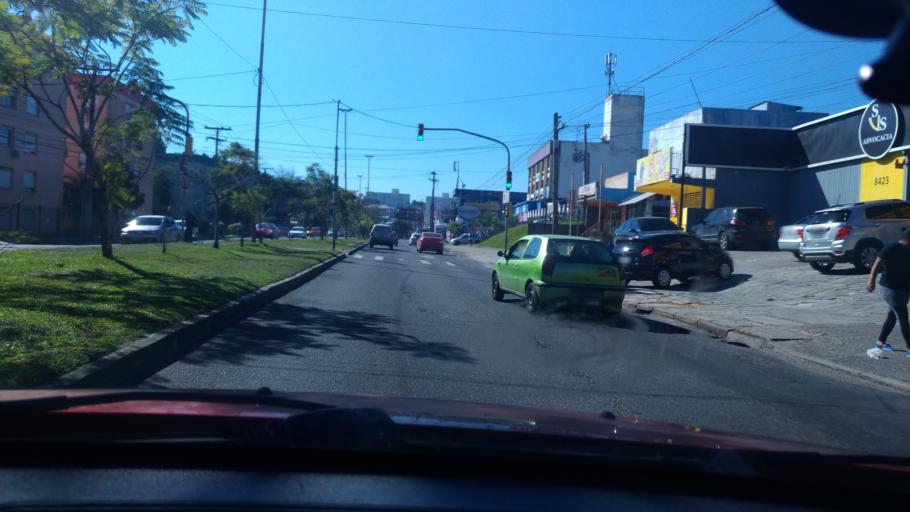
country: BR
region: Rio Grande do Sul
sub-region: Cachoeirinha
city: Cachoeirinha
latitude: -30.0402
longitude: -51.1279
